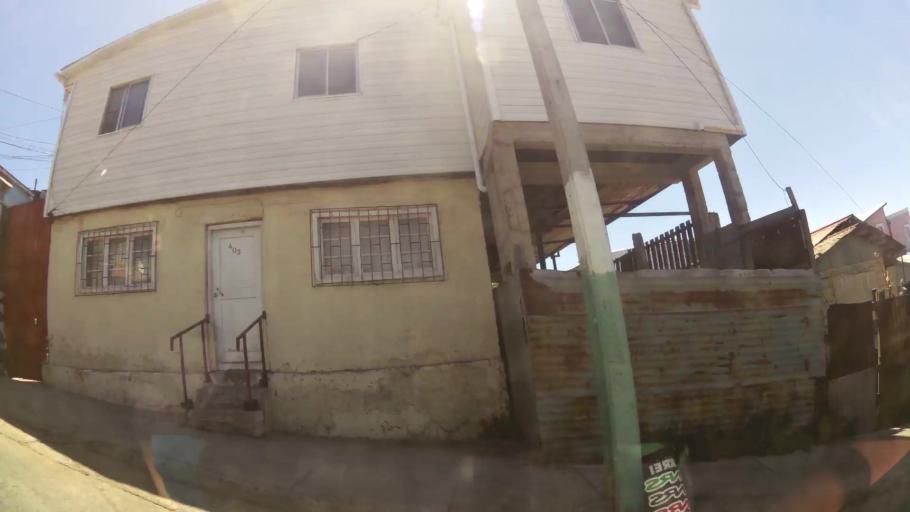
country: CL
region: Valparaiso
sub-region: Provincia de Valparaiso
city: Valparaiso
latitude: -33.0545
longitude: -71.6374
